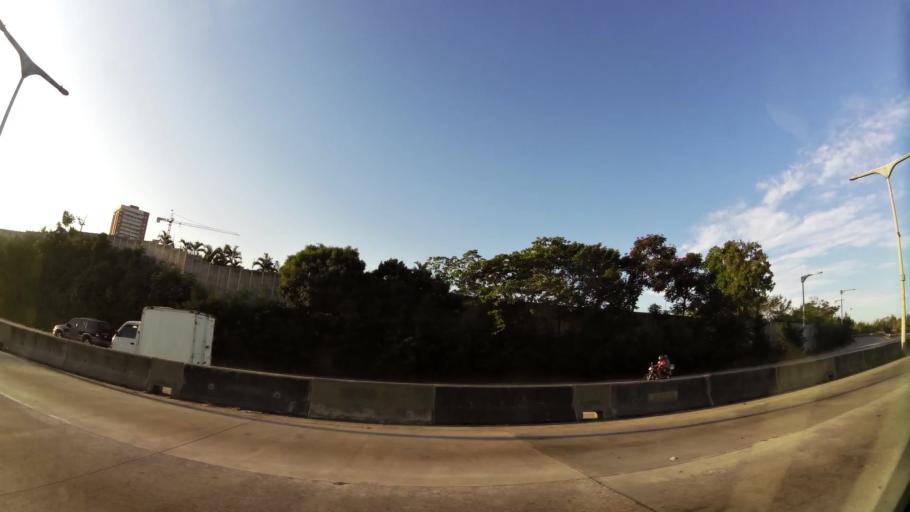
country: SV
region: La Libertad
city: Antiguo Cuscatlan
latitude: 13.6849
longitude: -89.2487
